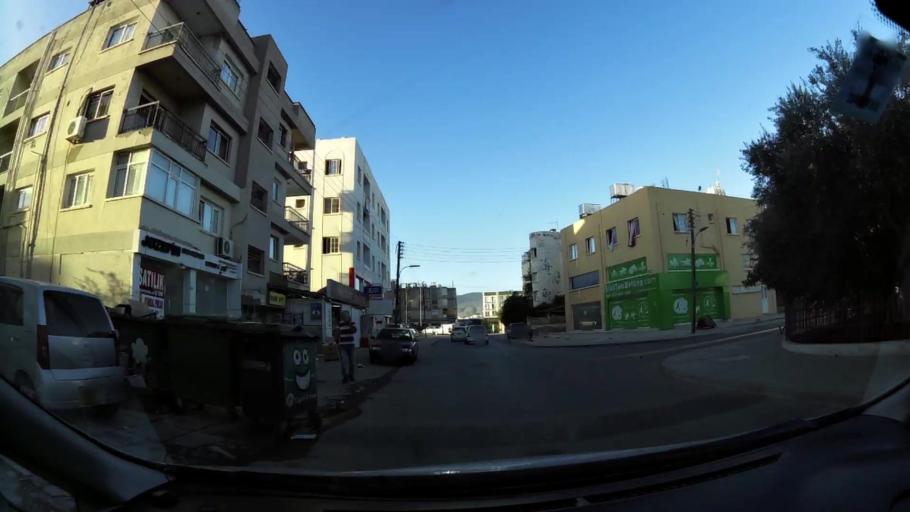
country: CY
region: Lefkosia
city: Nicosia
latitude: 35.2078
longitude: 33.3182
